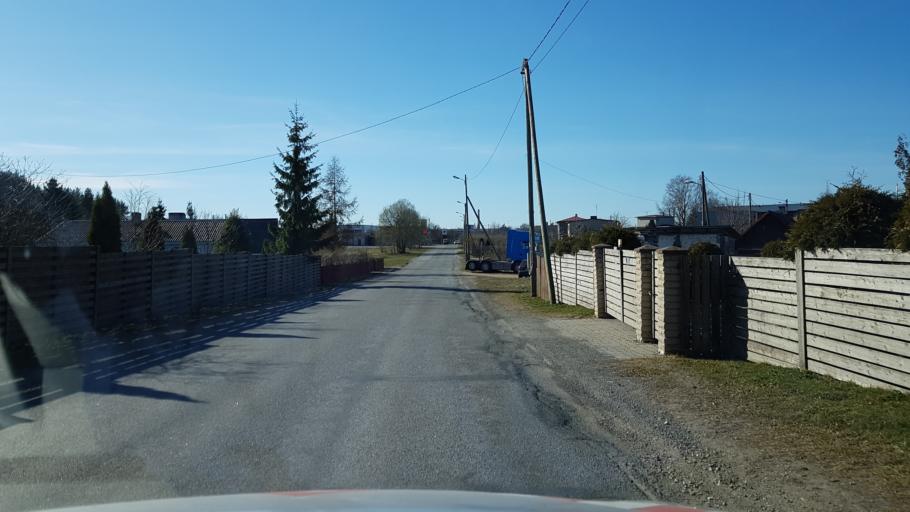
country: EE
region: Laeaene-Virumaa
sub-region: Rakvere linn
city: Rakvere
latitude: 59.3366
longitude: 26.3905
